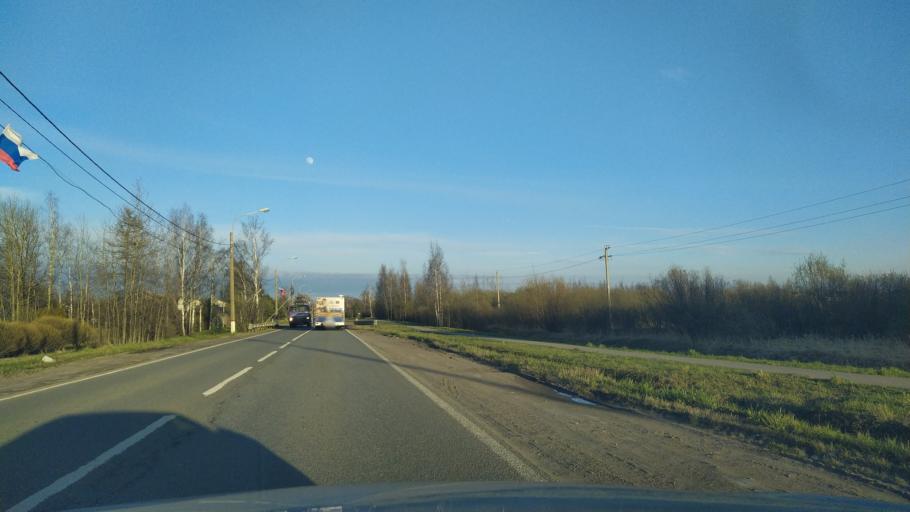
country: RU
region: St.-Petersburg
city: Aleksandrovskaya
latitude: 59.7378
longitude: 30.3249
